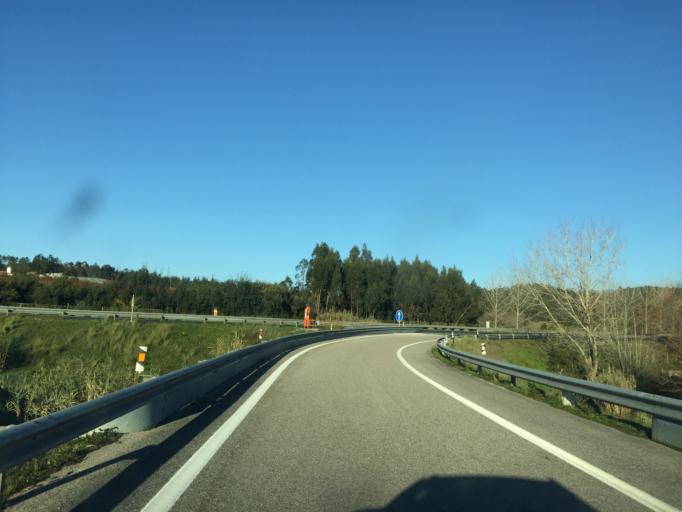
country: PT
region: Coimbra
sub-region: Figueira da Foz
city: Alhadas
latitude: 40.1532
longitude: -8.7931
